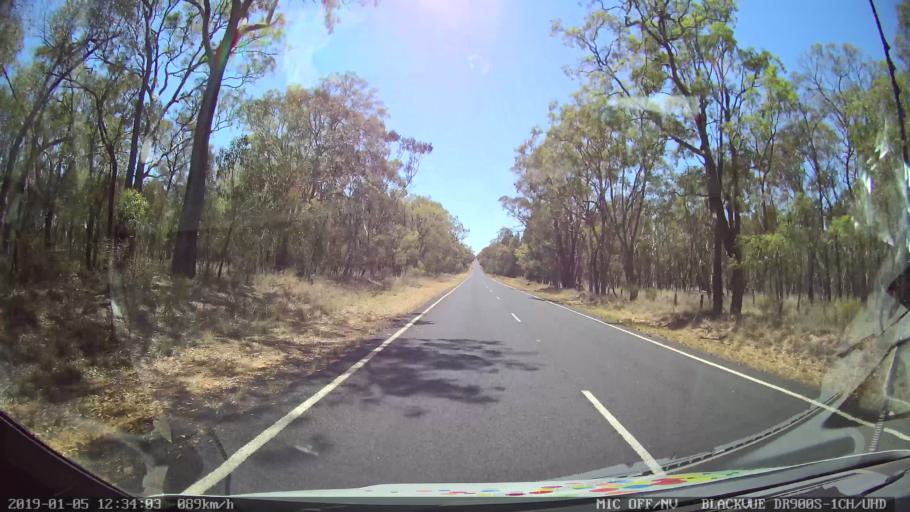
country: AU
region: New South Wales
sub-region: Warrumbungle Shire
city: Coonabarabran
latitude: -31.2132
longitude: 149.4041
